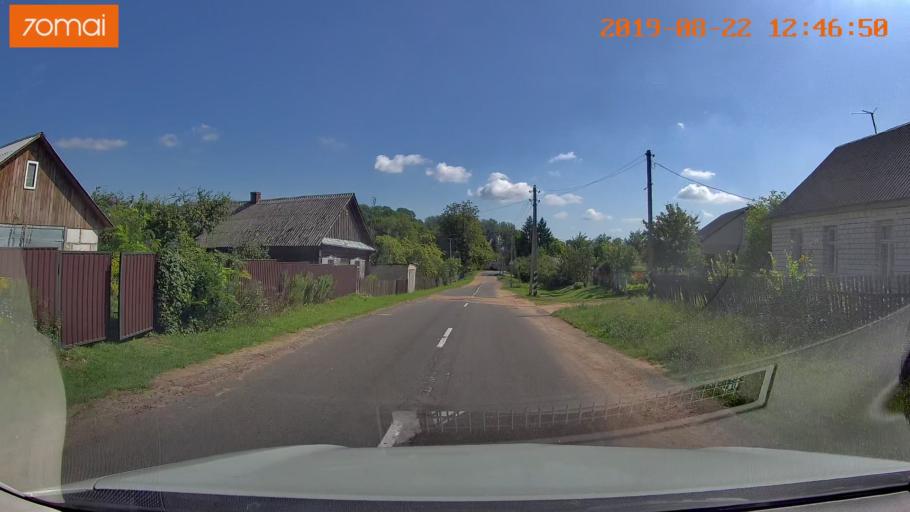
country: BY
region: Minsk
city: Prawdzinski
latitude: 53.4581
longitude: 27.6341
